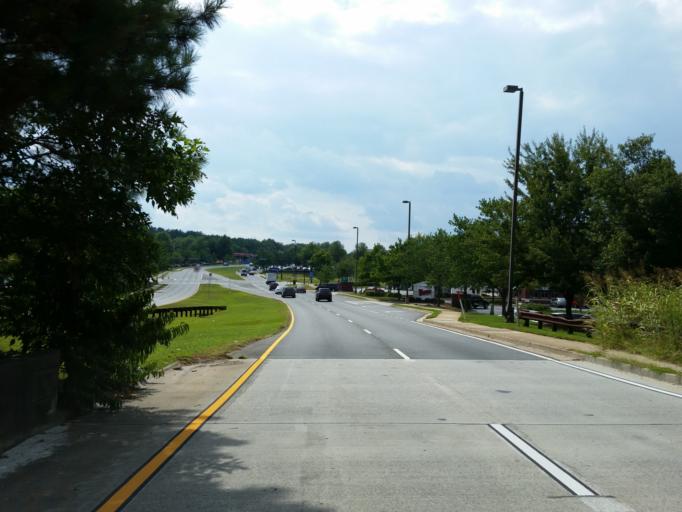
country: US
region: Georgia
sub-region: Fulton County
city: Alpharetta
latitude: 34.0405
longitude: -84.3170
